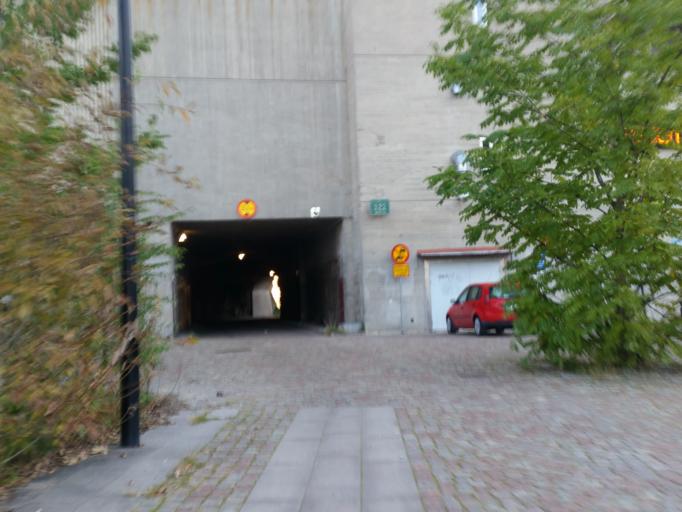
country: SE
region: Stockholm
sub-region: Stockholms Kommun
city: OEstermalm
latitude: 59.3135
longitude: 18.1037
